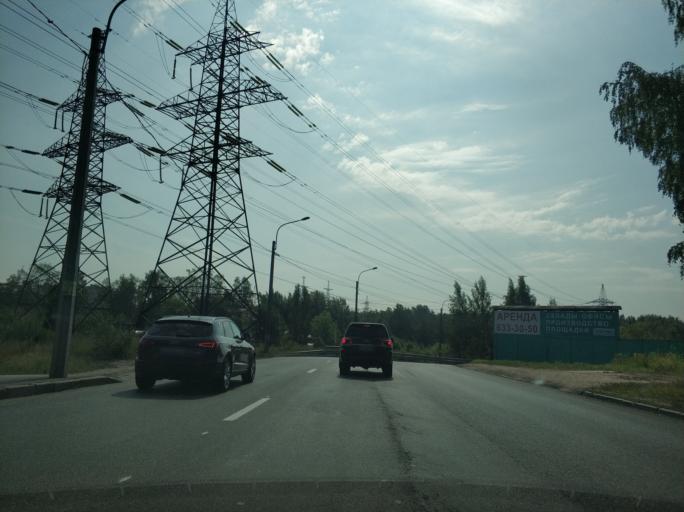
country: RU
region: St.-Petersburg
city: Krasnogvargeisky
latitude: 59.9771
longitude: 30.4996
